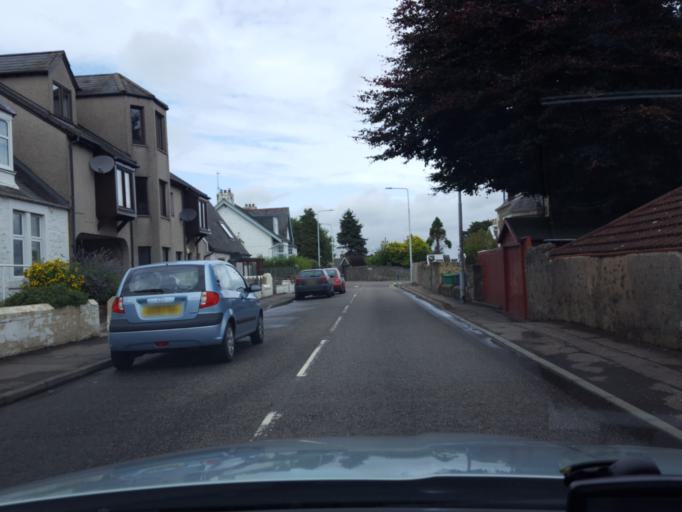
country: GB
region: Scotland
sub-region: Fife
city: Tayport
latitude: 56.4497
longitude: -2.8826
